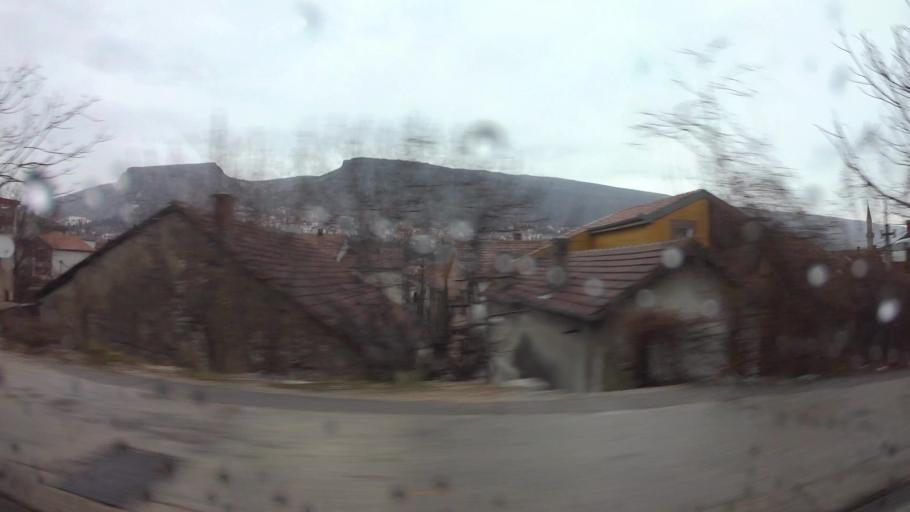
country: BA
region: Federation of Bosnia and Herzegovina
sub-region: Hercegovacko-Bosanski Kanton
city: Mostar
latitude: 43.3320
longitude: 17.8150
